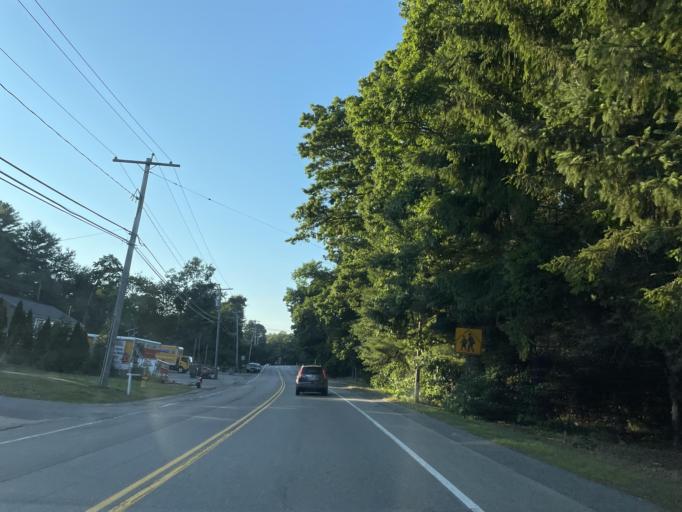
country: US
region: Massachusetts
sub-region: Plymouth County
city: Halifax
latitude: 42.0319
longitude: -70.8438
